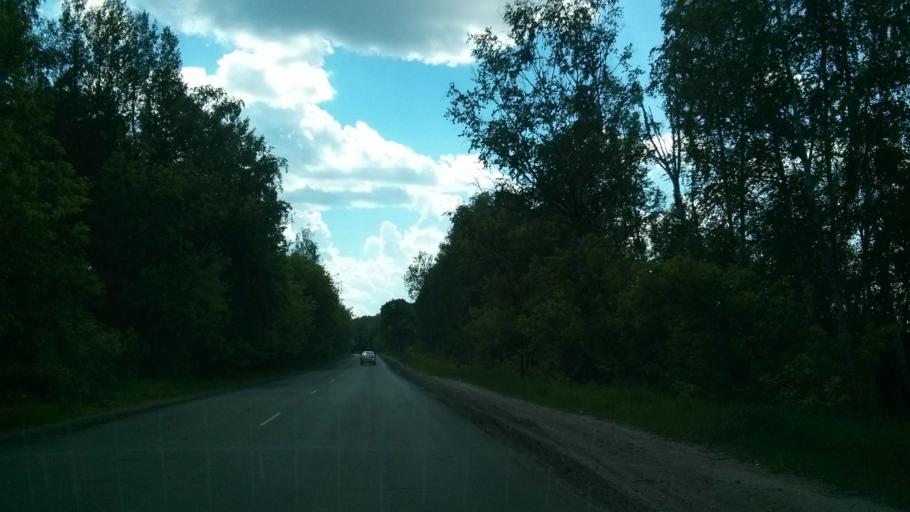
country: RU
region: Vladimir
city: Murom
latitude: 55.5476
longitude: 41.9949
